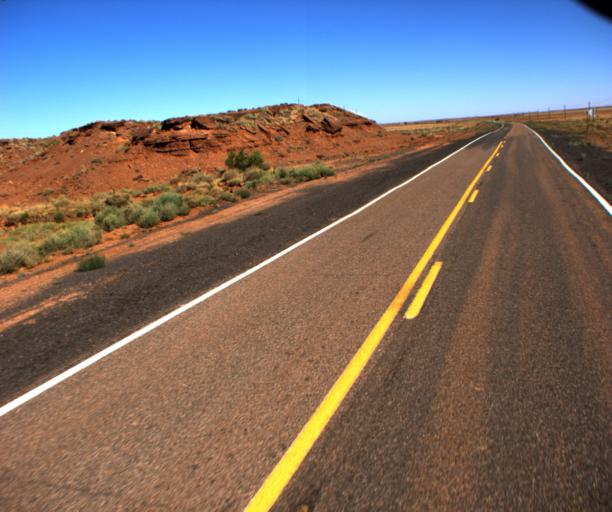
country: US
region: Arizona
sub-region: Coconino County
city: LeChee
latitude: 35.1413
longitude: -110.8915
